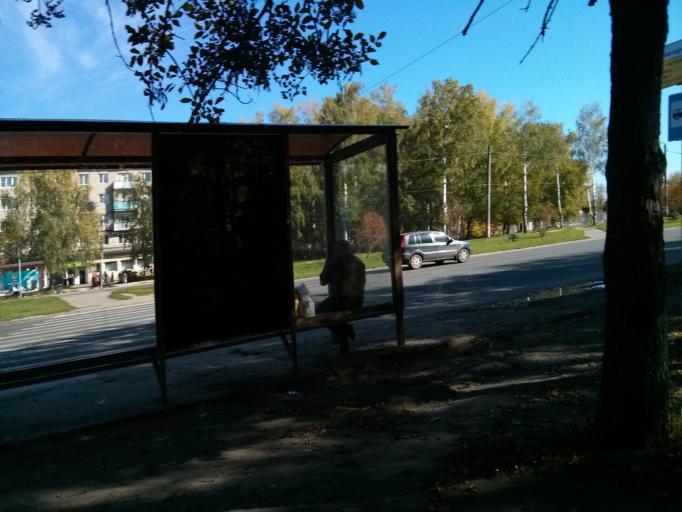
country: RU
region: Vladimir
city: Murom
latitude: 55.5488
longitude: 42.0635
